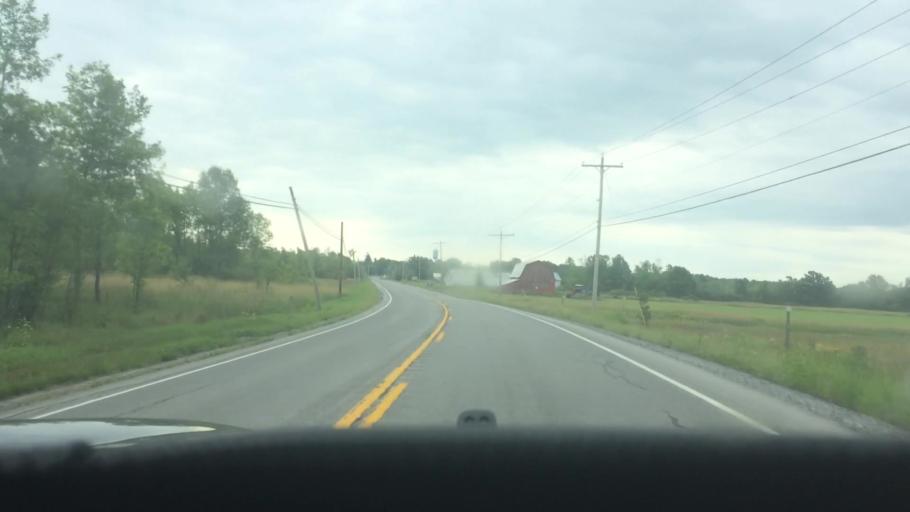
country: US
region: New York
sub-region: St. Lawrence County
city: Ogdensburg
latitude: 44.6280
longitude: -75.4205
